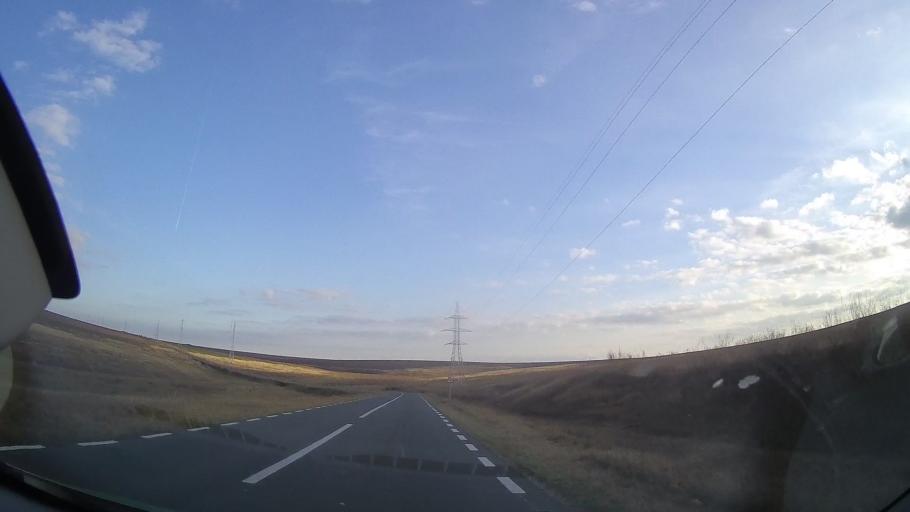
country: RO
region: Constanta
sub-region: Comuna Chirnogeni
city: Plopeni
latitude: 43.9552
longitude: 28.1501
